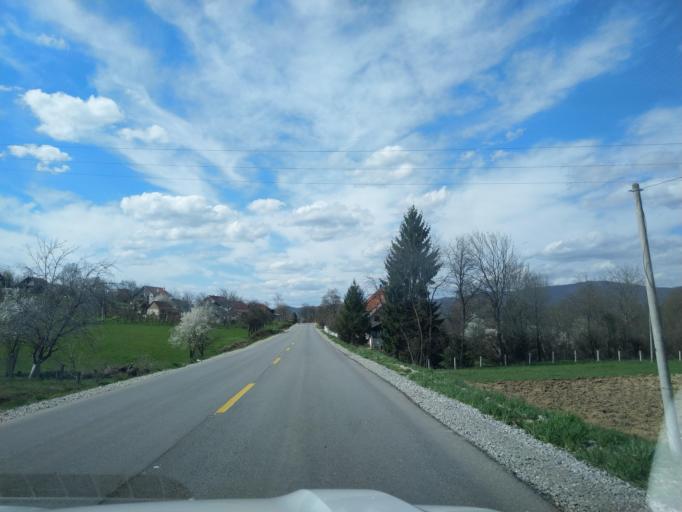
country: RS
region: Central Serbia
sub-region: Zlatiborski Okrug
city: Pozega
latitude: 43.8198
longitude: 20.0854
